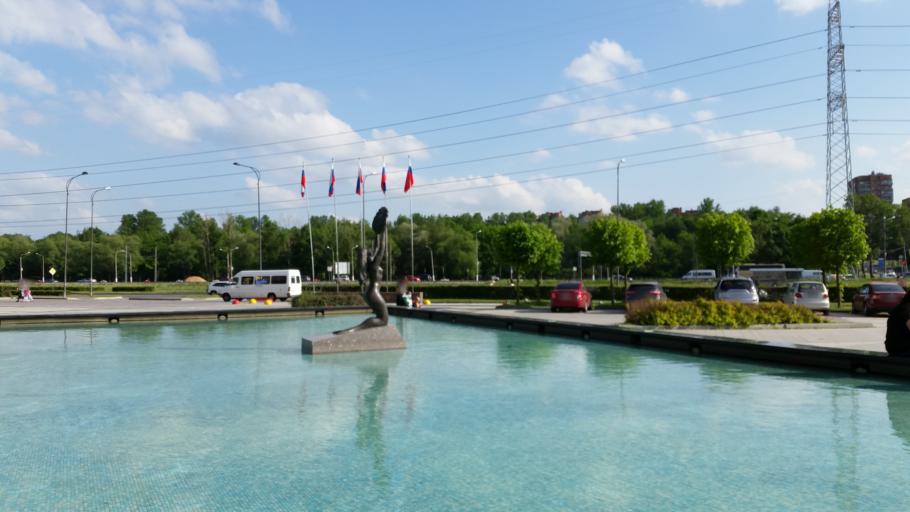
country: RU
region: St.-Petersburg
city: Sosnovaya Polyana
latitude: 59.8484
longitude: 30.1481
